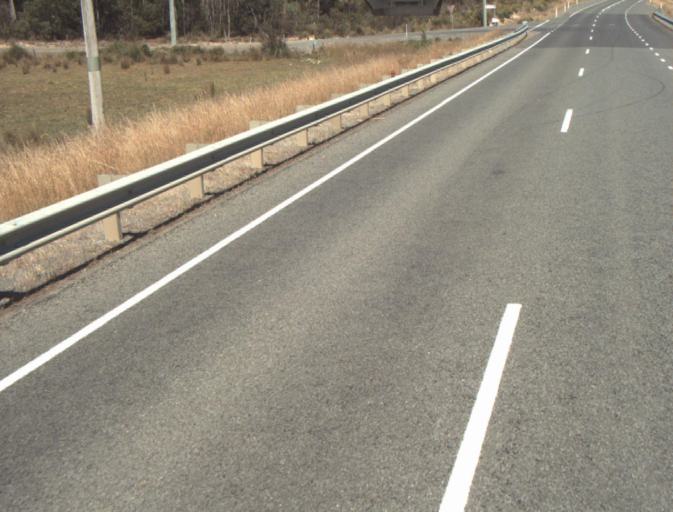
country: AU
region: Tasmania
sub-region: Launceston
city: Newstead
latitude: -41.3413
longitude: 147.3461
